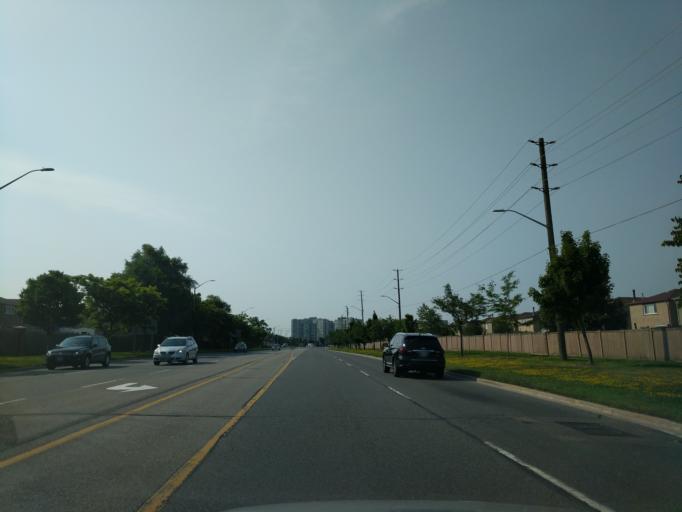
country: CA
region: Ontario
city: Markham
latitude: 43.8343
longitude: -79.2761
